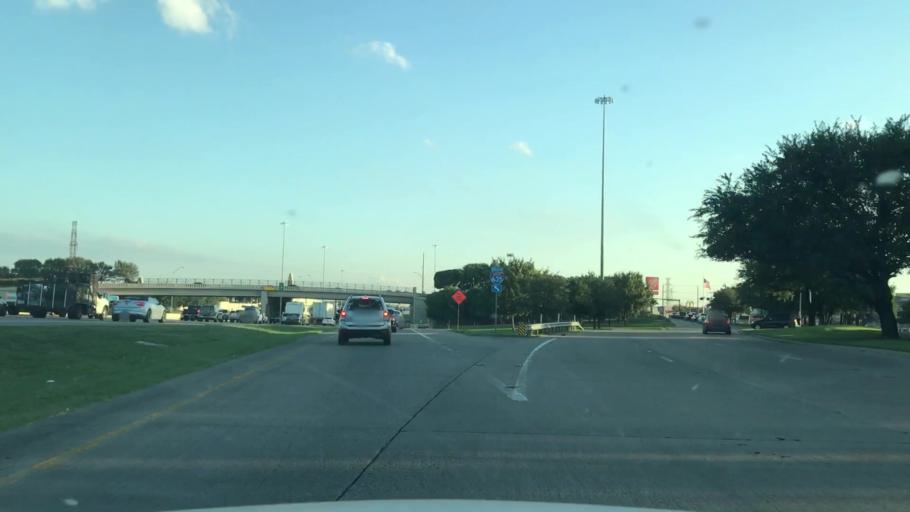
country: US
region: Texas
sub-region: Dallas County
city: Mesquite
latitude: 32.8039
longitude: -96.6272
